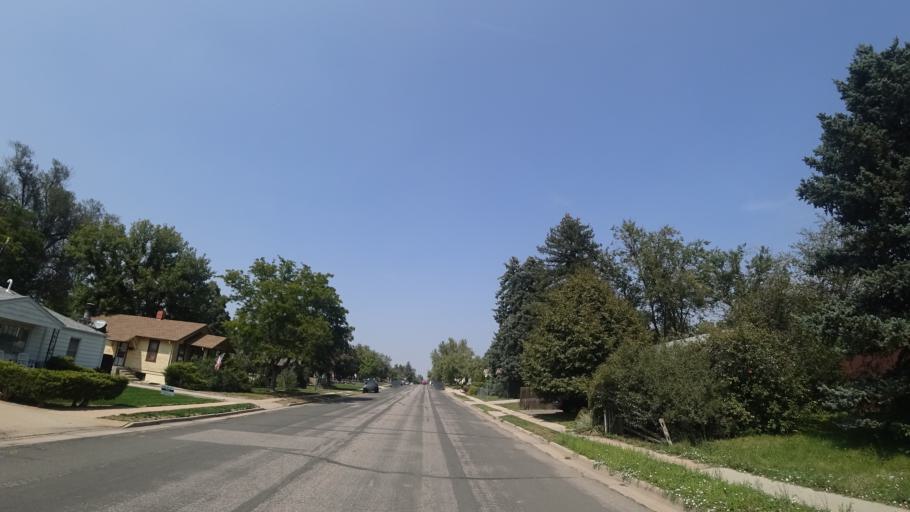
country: US
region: Colorado
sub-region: Arapahoe County
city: Englewood
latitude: 39.6369
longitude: -104.9924
